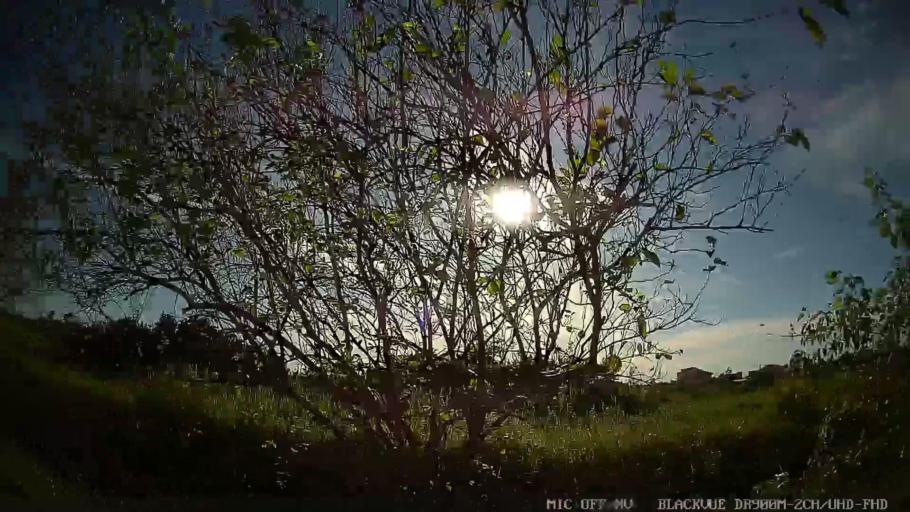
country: BR
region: Sao Paulo
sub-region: Iguape
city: Iguape
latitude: -24.7581
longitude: -47.5727
